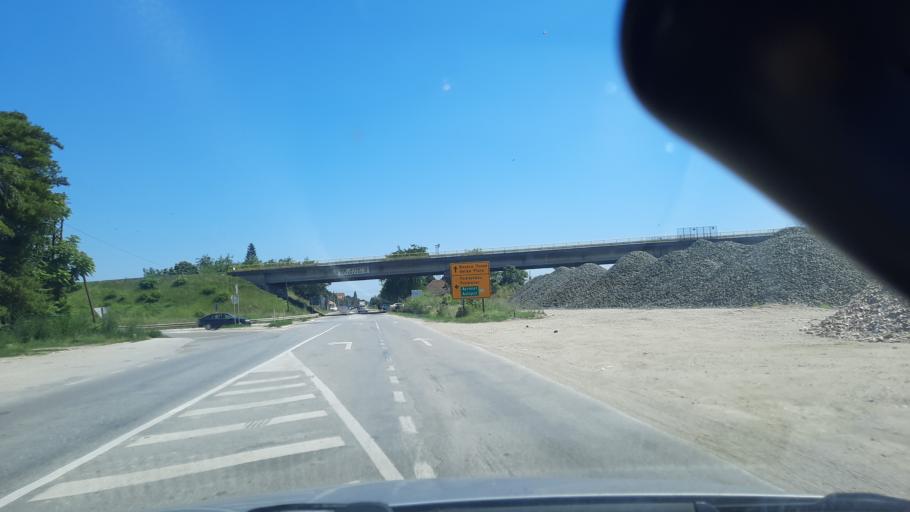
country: RS
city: Lugavcina
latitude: 44.5892
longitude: 20.9987
